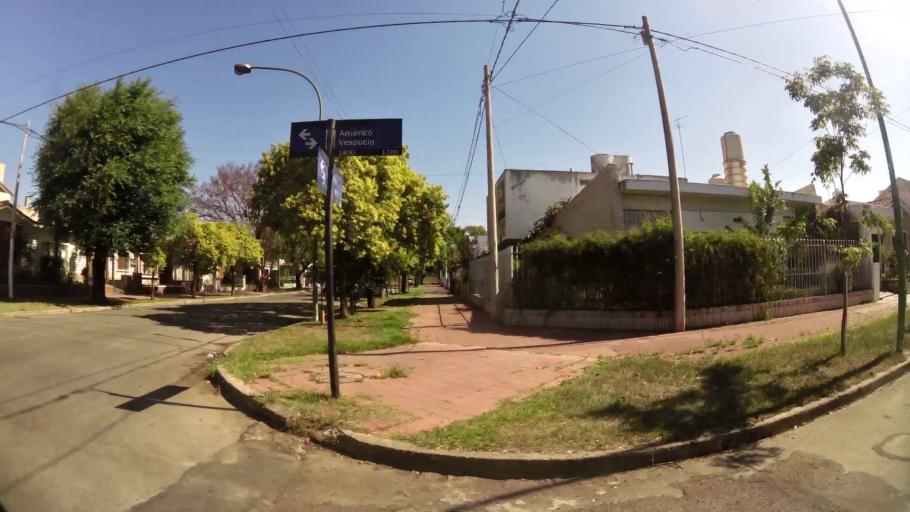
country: AR
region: Cordoba
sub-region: Departamento de Capital
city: Cordoba
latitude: -31.4206
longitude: -64.1608
